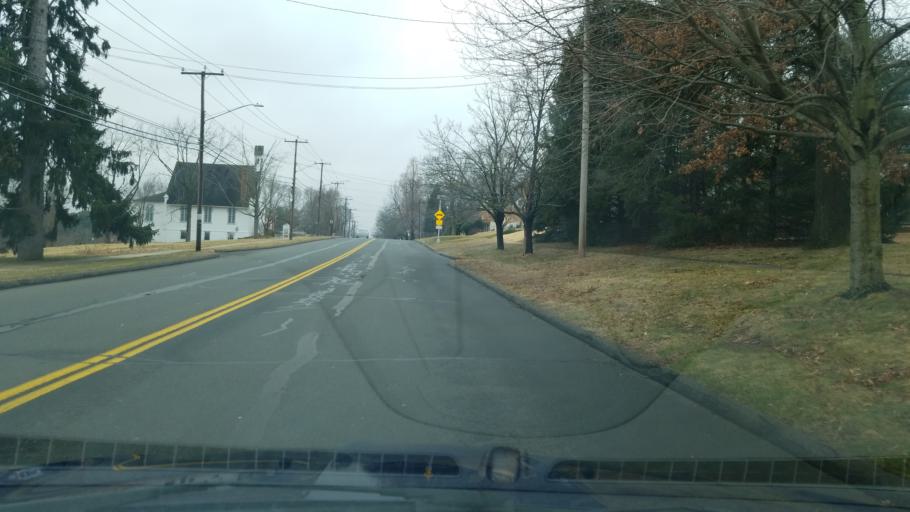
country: US
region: Connecticut
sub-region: Hartford County
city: Wethersfield
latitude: 41.6889
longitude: -72.6715
